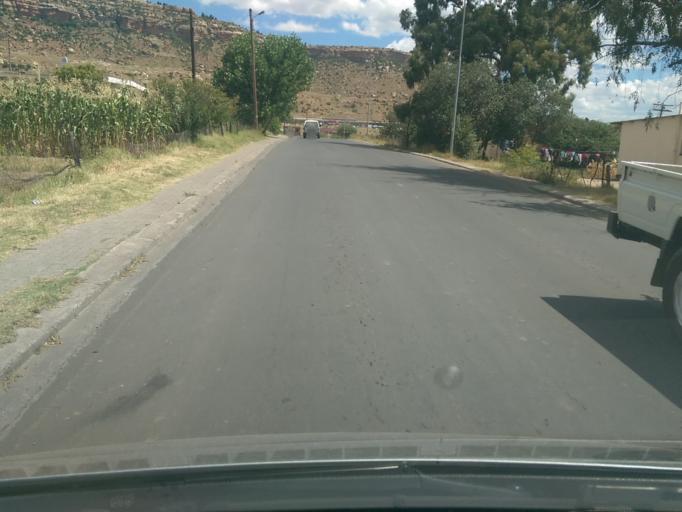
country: LS
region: Maseru
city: Maseru
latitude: -29.3290
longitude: 27.4867
